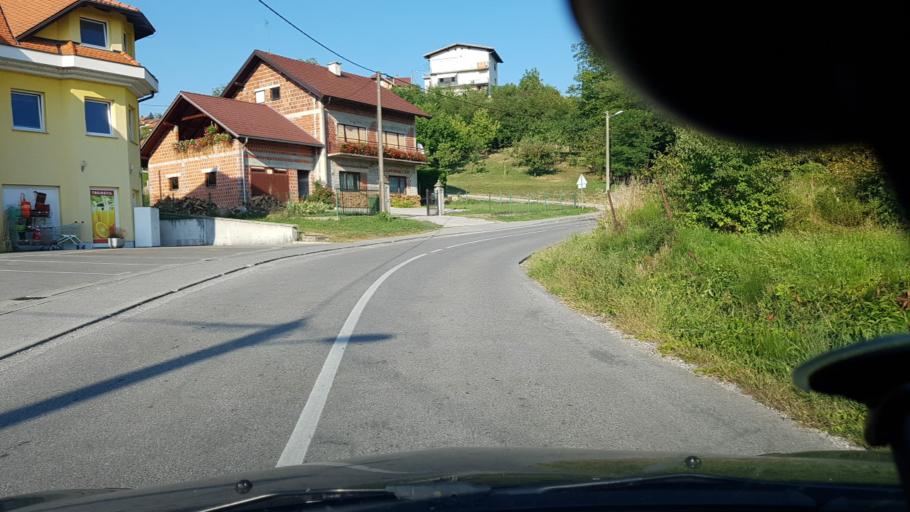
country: SI
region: Bistrica ob Sotli
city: Bistrica ob Sotli
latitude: 46.0471
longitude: 15.7337
